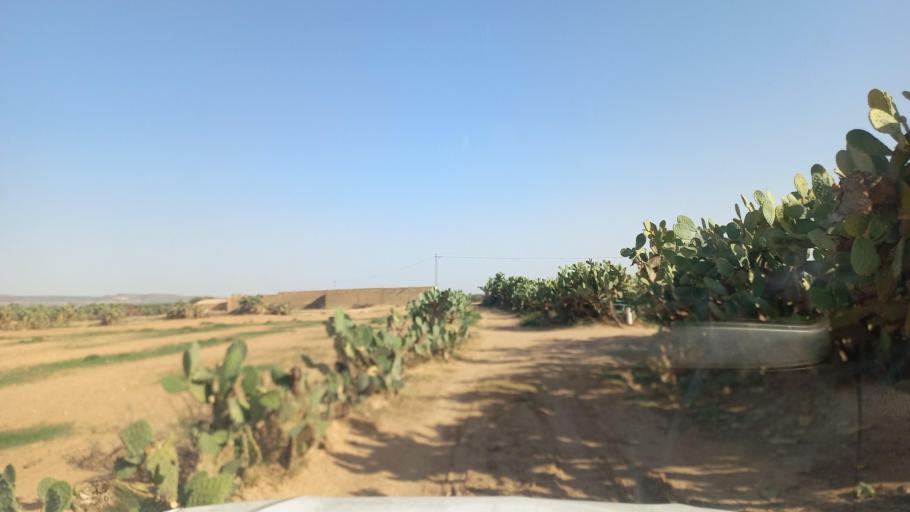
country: TN
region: Al Qasrayn
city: Sbiba
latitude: 35.3214
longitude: 9.0245
